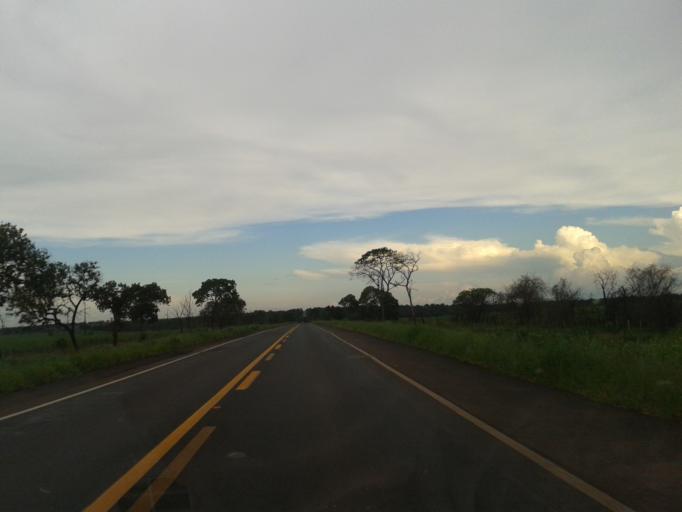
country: BR
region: Minas Gerais
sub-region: Santa Vitoria
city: Santa Vitoria
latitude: -18.8943
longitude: -50.1732
